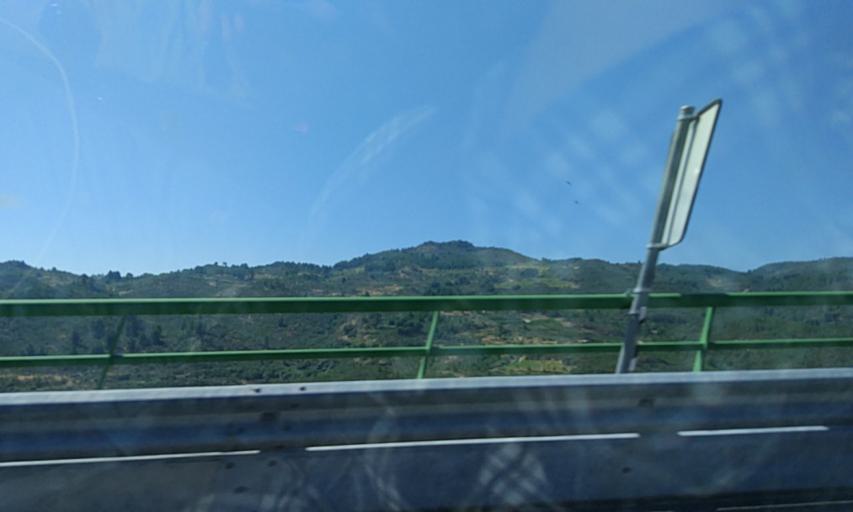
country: PT
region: Vila Real
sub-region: Murca
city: Murca
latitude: 41.3908
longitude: -7.4515
